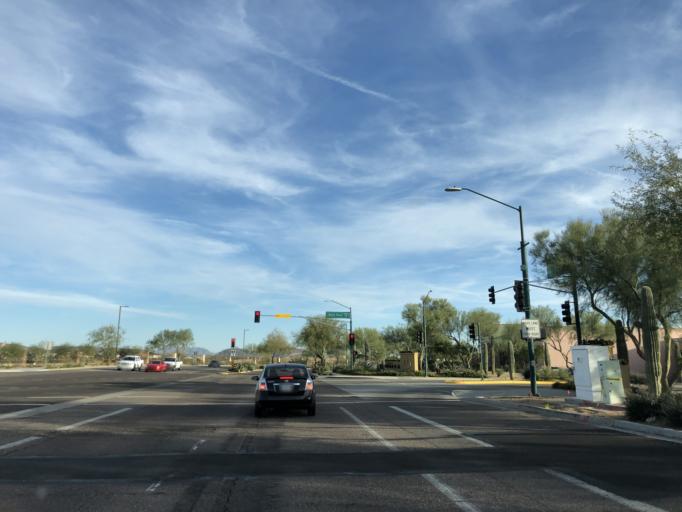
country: US
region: Arizona
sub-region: Maricopa County
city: Anthem
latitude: 33.7155
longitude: -112.1112
